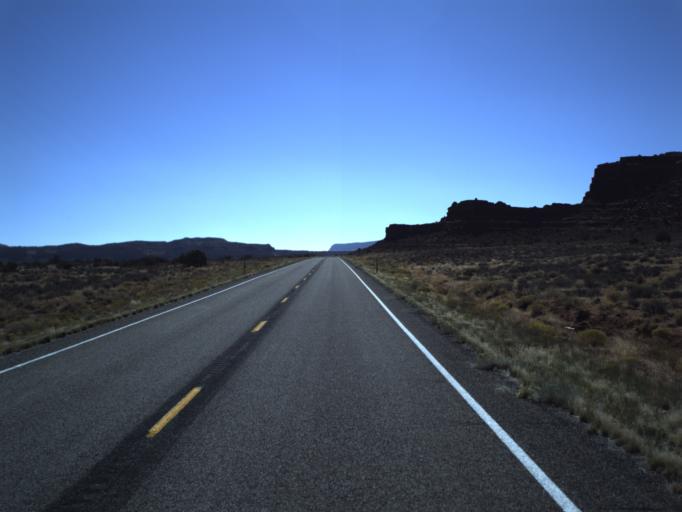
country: US
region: Utah
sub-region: San Juan County
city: Blanding
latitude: 37.7915
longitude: -110.2997
